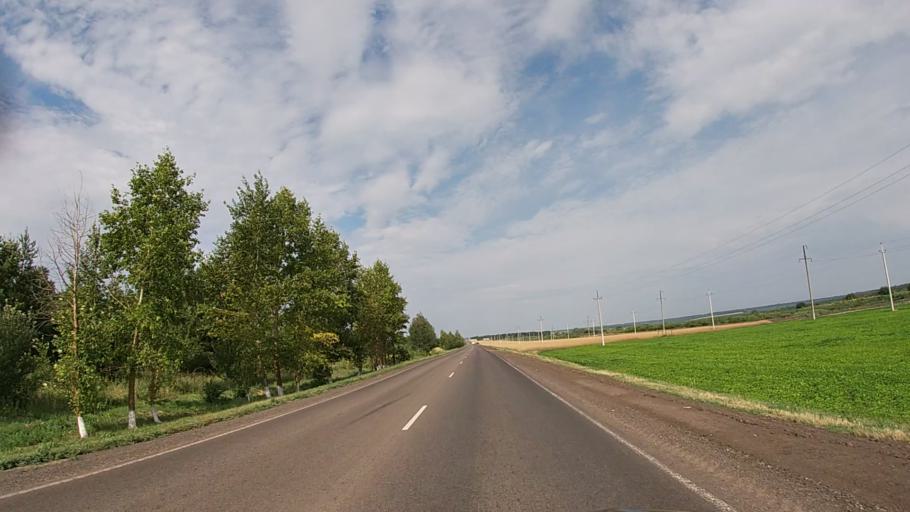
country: RU
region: Belgorod
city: Krasnaya Yaruga
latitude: 50.7979
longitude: 35.6228
